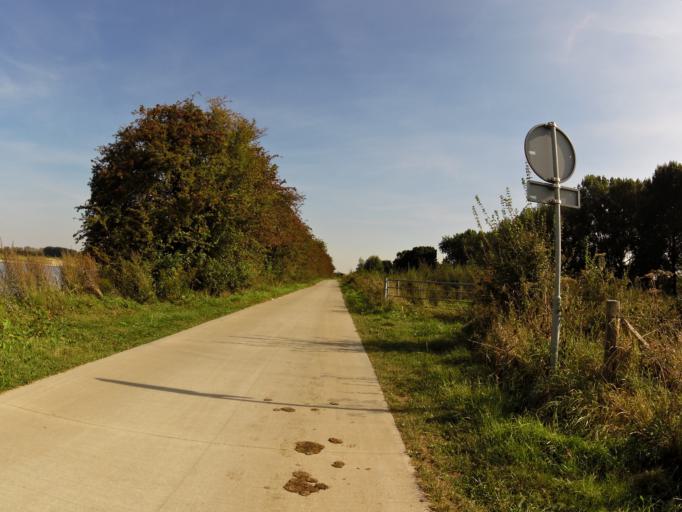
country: NL
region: Gelderland
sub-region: Gemeente Duiven
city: Duiven
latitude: 51.8788
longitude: 6.0188
